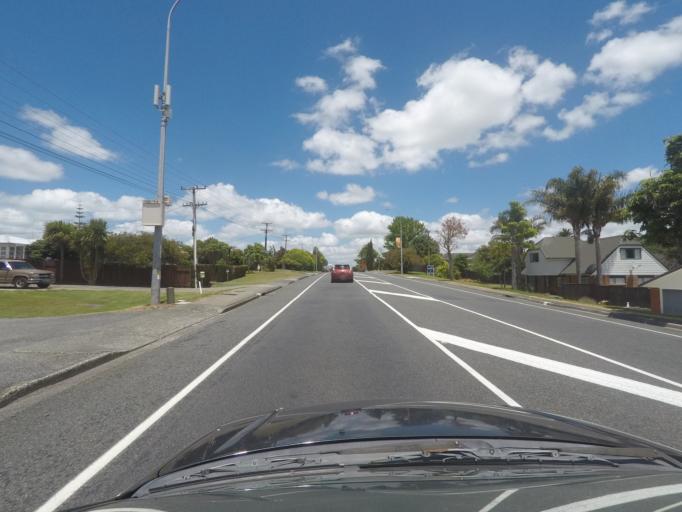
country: NZ
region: Northland
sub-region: Whangarei
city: Whangarei
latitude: -35.7470
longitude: 174.3673
